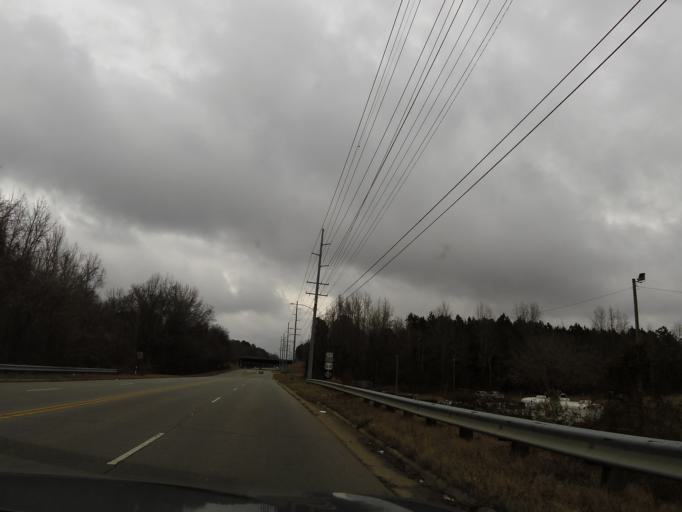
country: US
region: North Carolina
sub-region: Nash County
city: Rocky Mount
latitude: 35.9549
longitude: -77.7873
